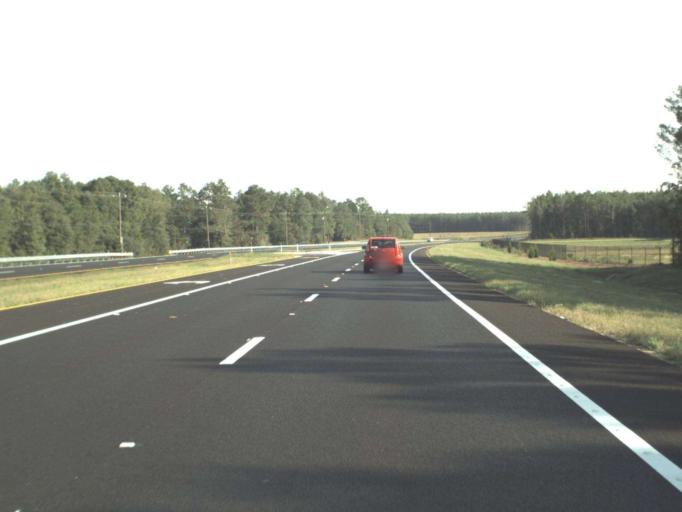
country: US
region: Florida
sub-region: Holmes County
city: Bonifay
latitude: 30.5381
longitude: -85.8343
